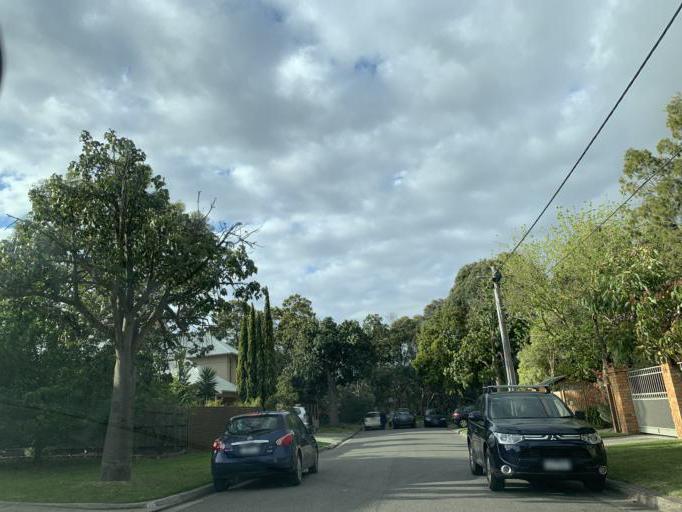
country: AU
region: Victoria
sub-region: Bayside
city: Cheltenham
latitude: -37.9772
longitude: 145.0425
